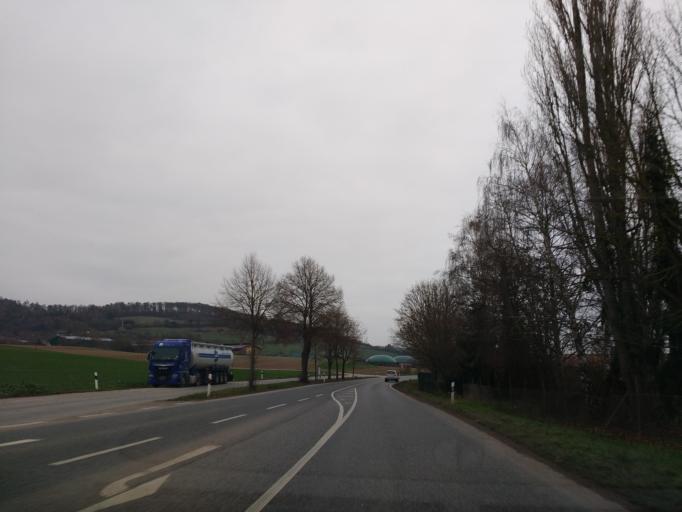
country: DE
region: Hesse
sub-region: Regierungsbezirk Kassel
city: Alheim
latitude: 51.0417
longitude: 9.6737
